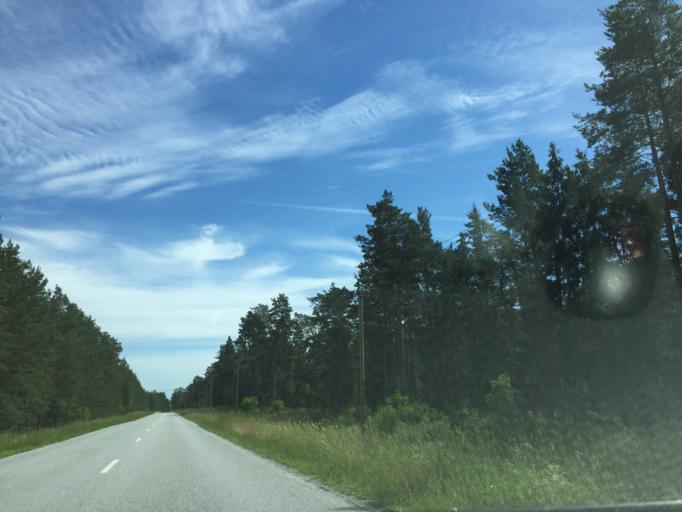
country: LV
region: Rojas
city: Roja
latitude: 57.5810
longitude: 22.6222
